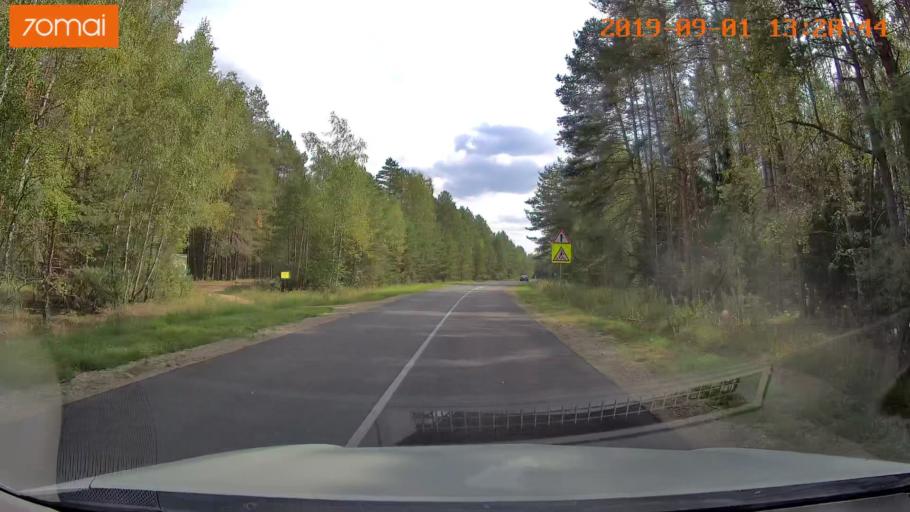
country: RU
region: Kaluga
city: Maloyaroslavets
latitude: 54.9104
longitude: 36.5044
